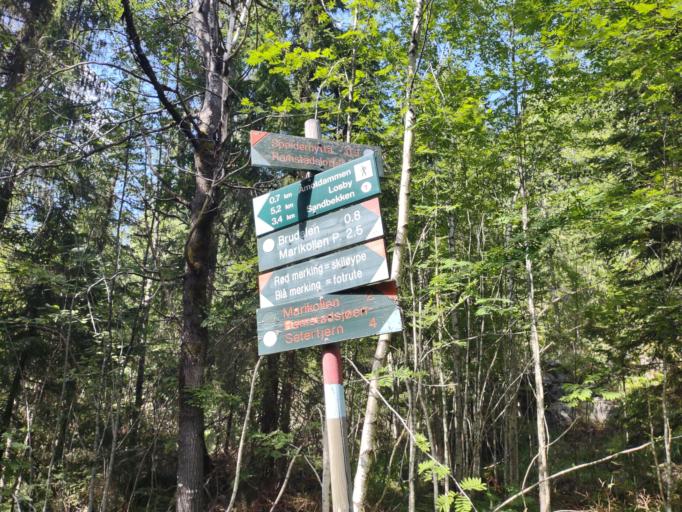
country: NO
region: Akershus
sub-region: Raelingen
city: Fjerdingby
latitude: 59.9109
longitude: 11.0470
